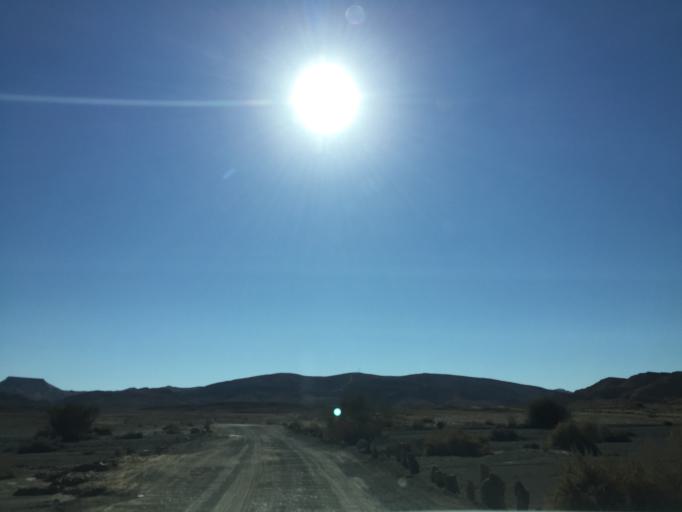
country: IL
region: Southern District
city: Mitzpe Ramon
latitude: 30.6027
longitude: 34.8964
